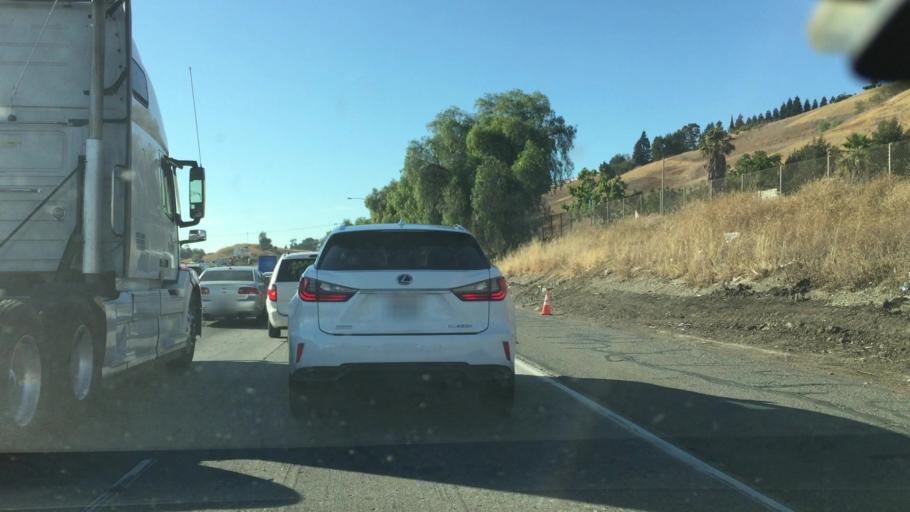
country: US
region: California
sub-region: Alameda County
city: Fremont
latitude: 37.5183
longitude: -121.9416
